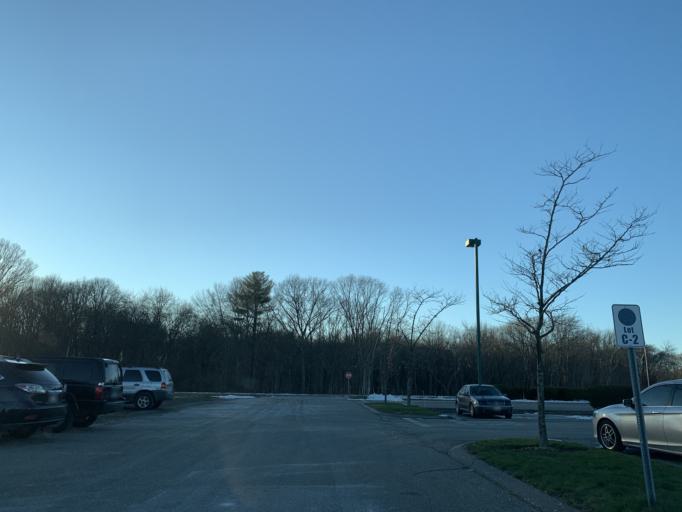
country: US
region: Rhode Island
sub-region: Kent County
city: West Warwick
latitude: 41.6603
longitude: -71.5031
